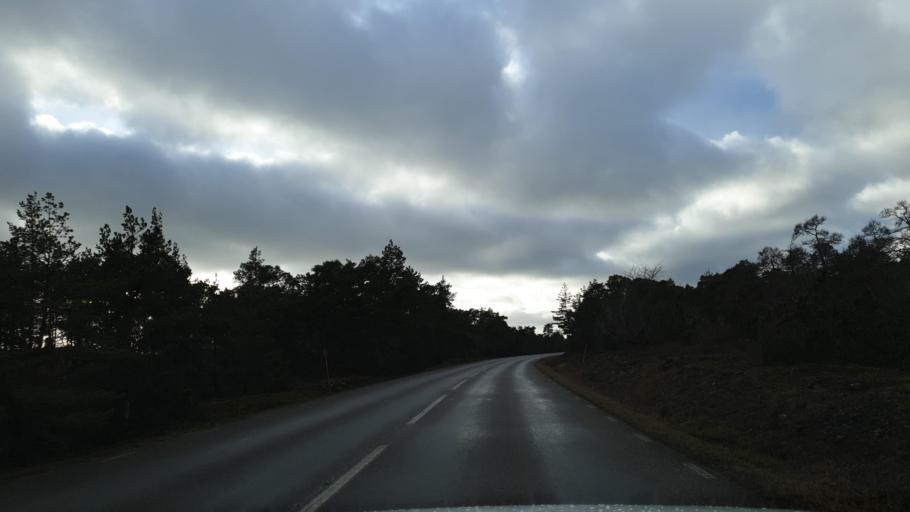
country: SE
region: Gotland
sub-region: Gotland
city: Slite
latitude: 57.4398
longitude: 18.6977
